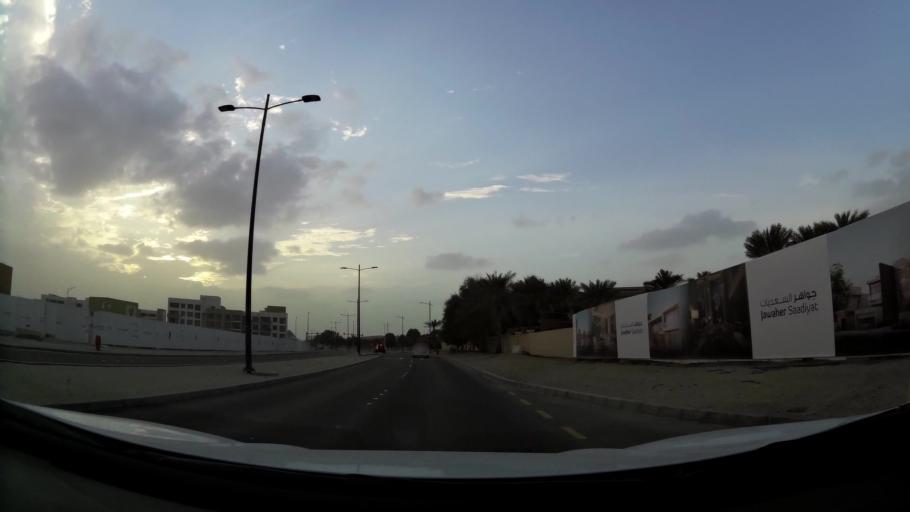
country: AE
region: Abu Dhabi
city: Abu Dhabi
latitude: 24.5333
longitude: 54.4233
